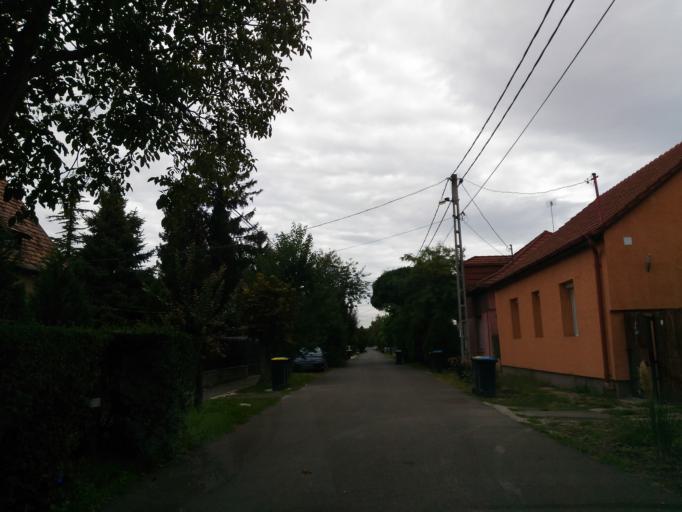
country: HU
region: Pest
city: Halasztelek
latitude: 47.3931
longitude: 18.9768
